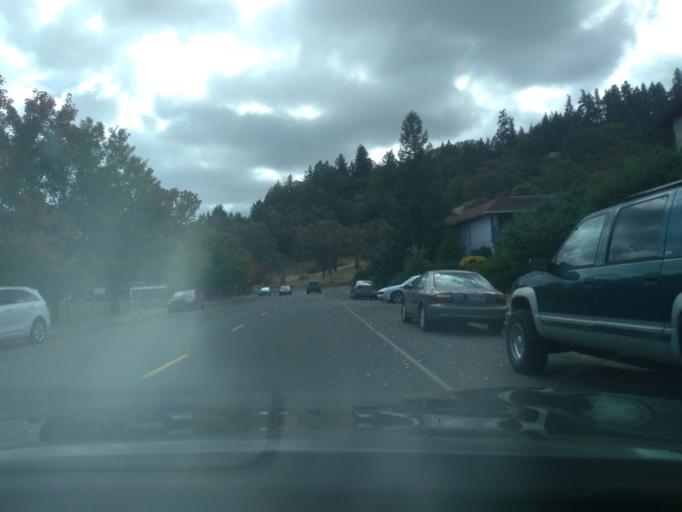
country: US
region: California
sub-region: Mendocino County
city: Ukiah
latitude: 39.1223
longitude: -123.2070
